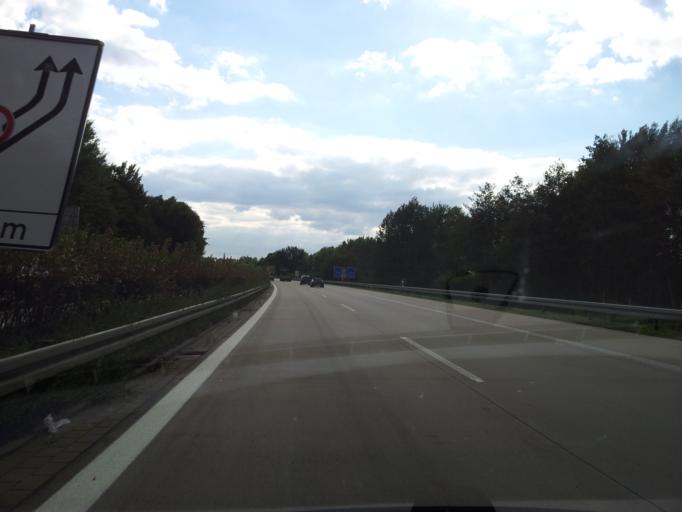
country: DE
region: Brandenburg
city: Schipkau
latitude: 51.5284
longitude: 13.9057
